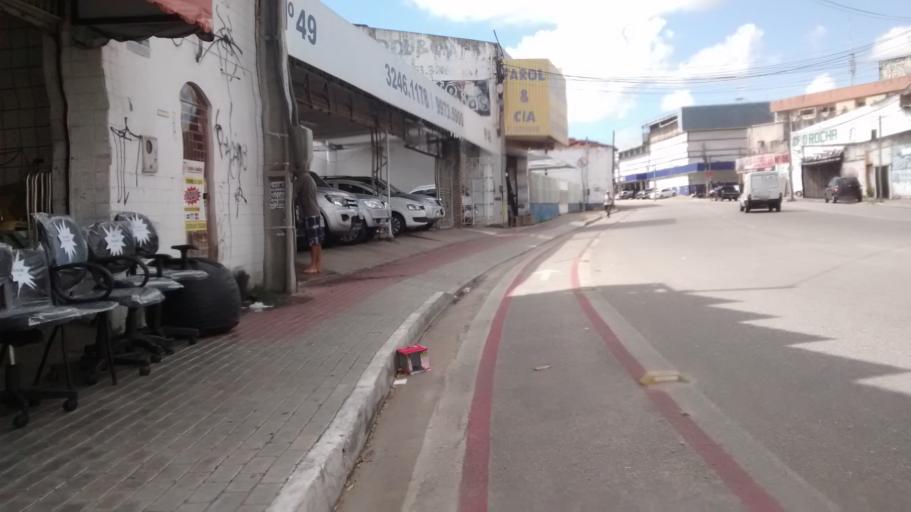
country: BR
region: Ceara
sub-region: Fortaleza
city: Fortaleza
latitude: -3.7386
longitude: -38.5233
